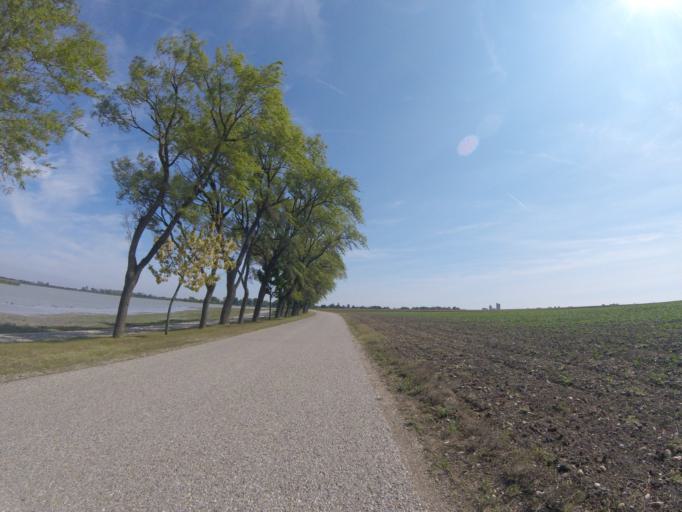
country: AT
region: Burgenland
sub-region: Politischer Bezirk Neusiedl am See
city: Sankt Andra am Zicksee
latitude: 47.7834
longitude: 16.9031
